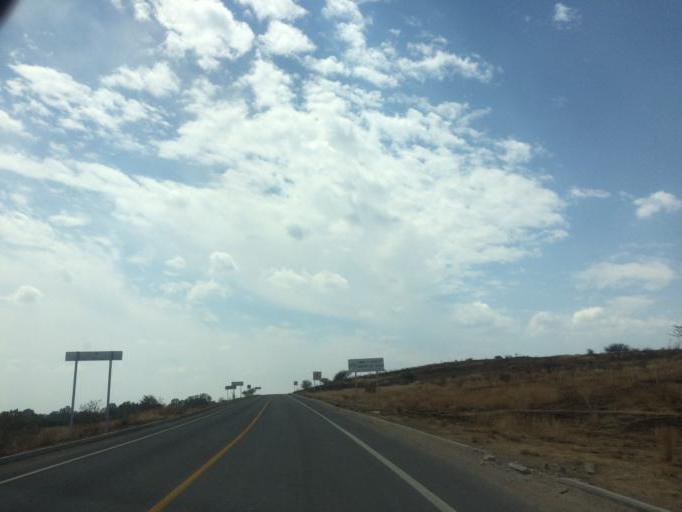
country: MX
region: Guanajuato
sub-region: Silao de la Victoria
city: Loma de Yerbabuena
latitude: 21.0320
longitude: -101.4728
